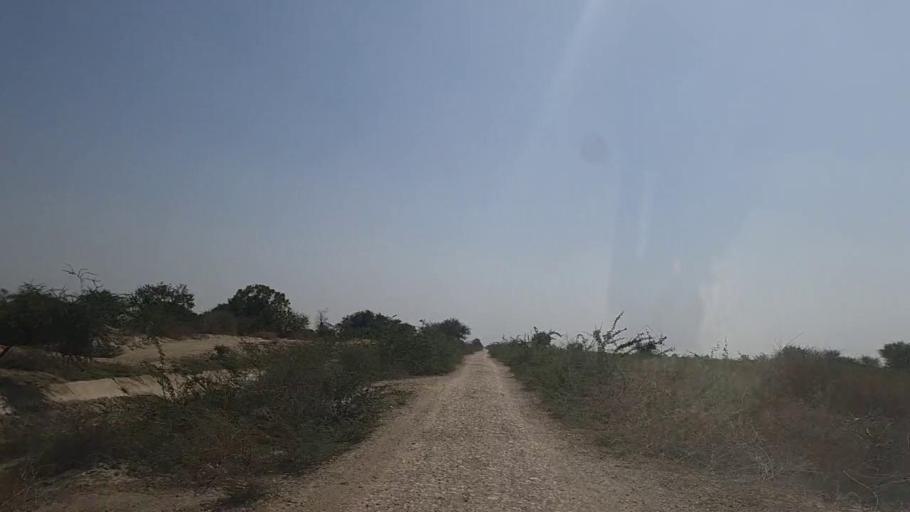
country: PK
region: Sindh
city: Naukot
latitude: 24.6494
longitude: 69.2764
